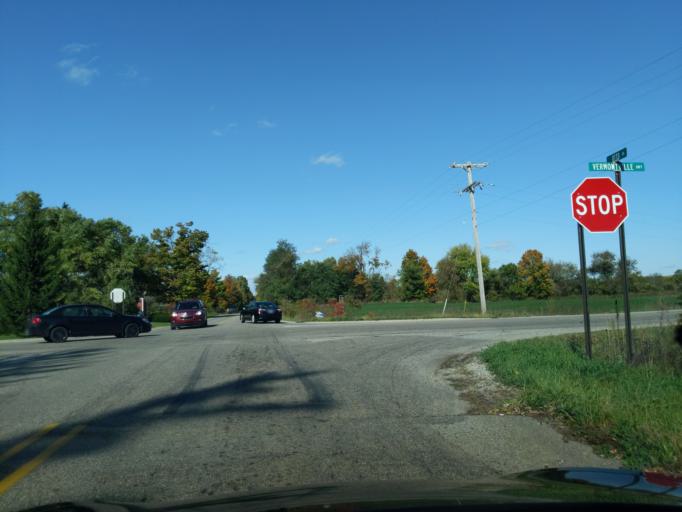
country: US
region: Michigan
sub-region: Eaton County
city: Potterville
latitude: 42.6258
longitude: -84.7977
